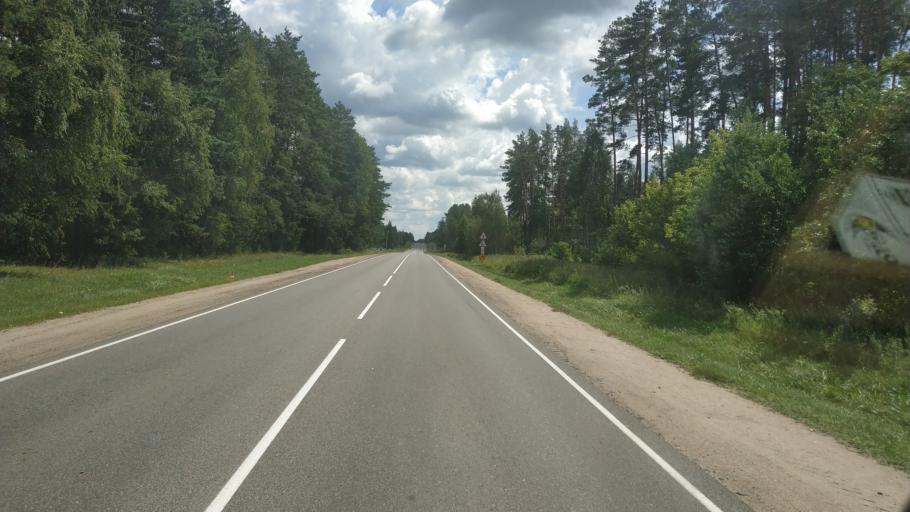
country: BY
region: Mogilev
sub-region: Mahilyowski Rayon
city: Veyno
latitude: 53.8300
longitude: 30.4099
